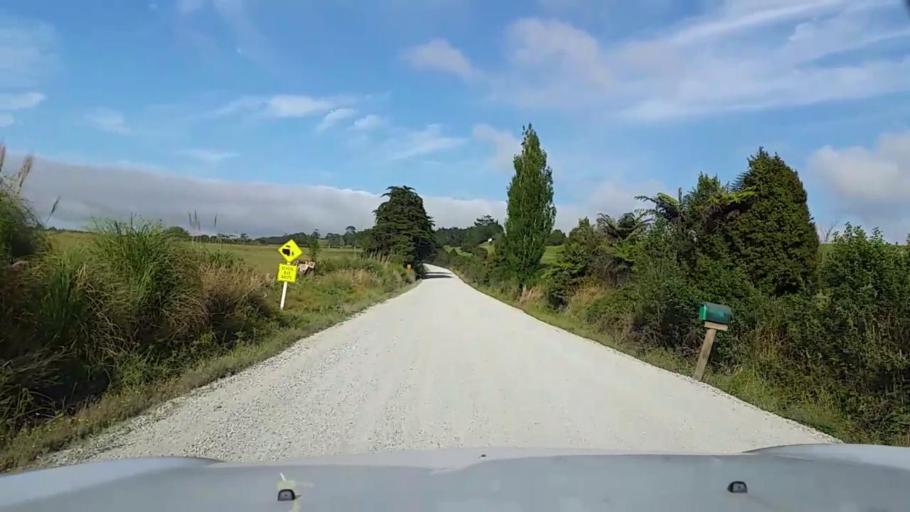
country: NZ
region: Northland
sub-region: Whangarei
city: Maungatapere
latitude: -35.6839
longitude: 174.1906
